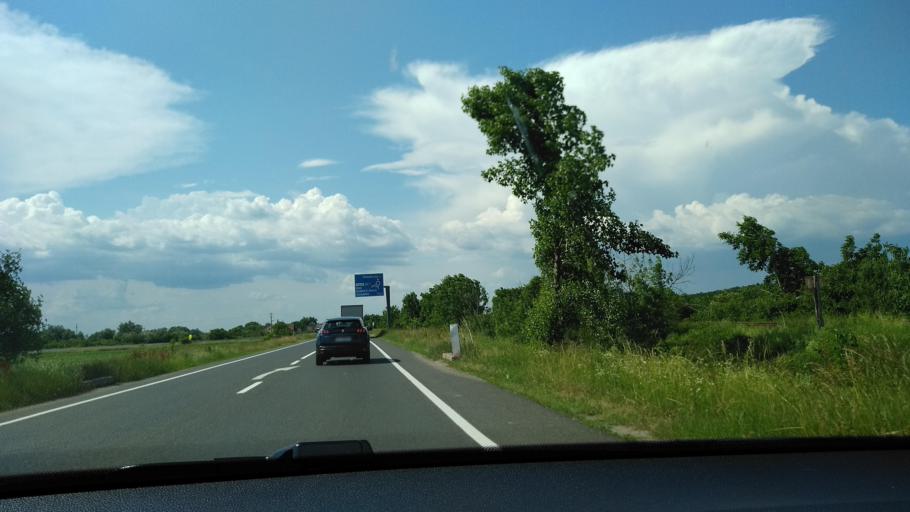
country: RO
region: Timis
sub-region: Comuna Costeiu
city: Costeiu
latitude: 45.7246
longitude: 21.8730
